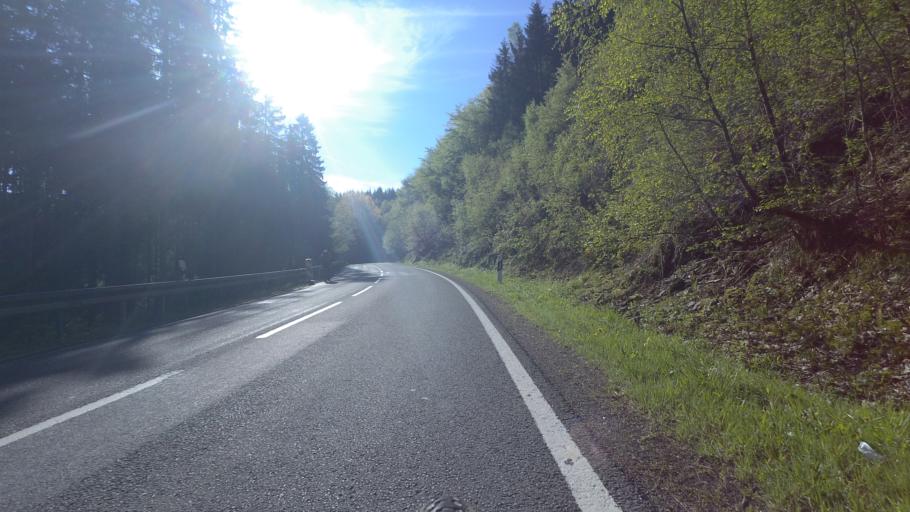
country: DE
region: Saxony-Anhalt
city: Darlingerode
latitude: 51.7842
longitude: 10.7395
